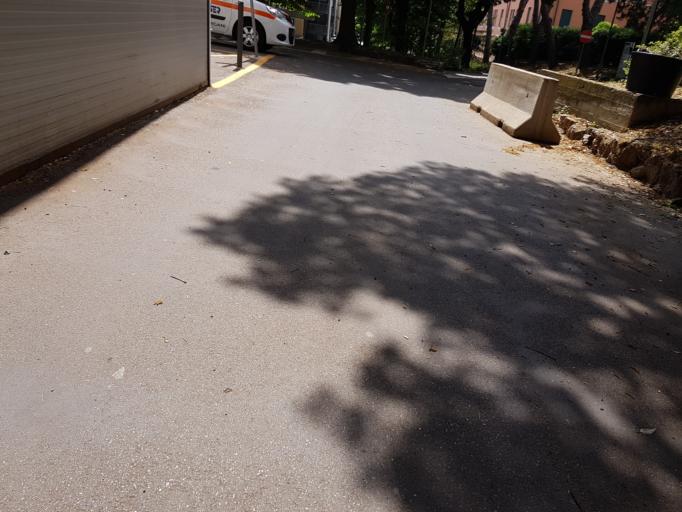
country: IT
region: Liguria
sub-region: Provincia di Genova
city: Genoa
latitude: 44.4097
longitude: 8.9704
